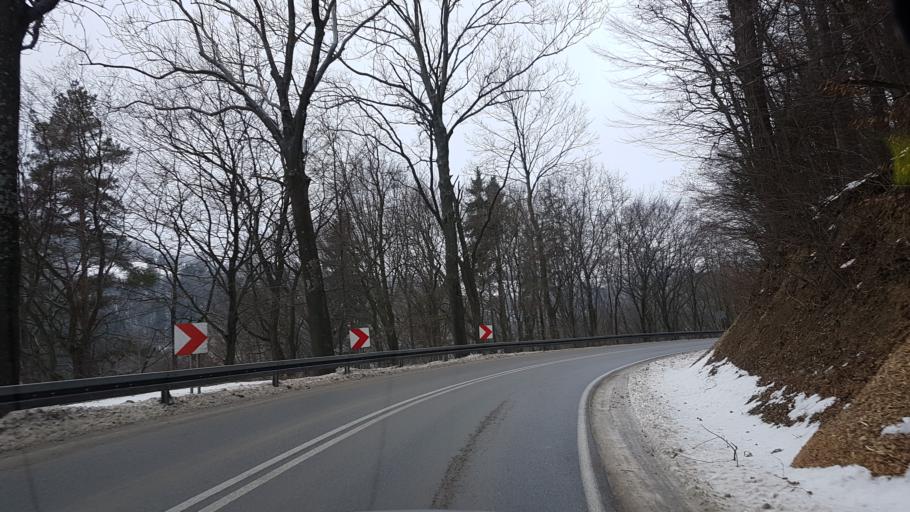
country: PL
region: Lesser Poland Voivodeship
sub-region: Powiat nowosadecki
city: Piwniczna-Zdroj
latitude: 49.4037
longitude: 20.7458
